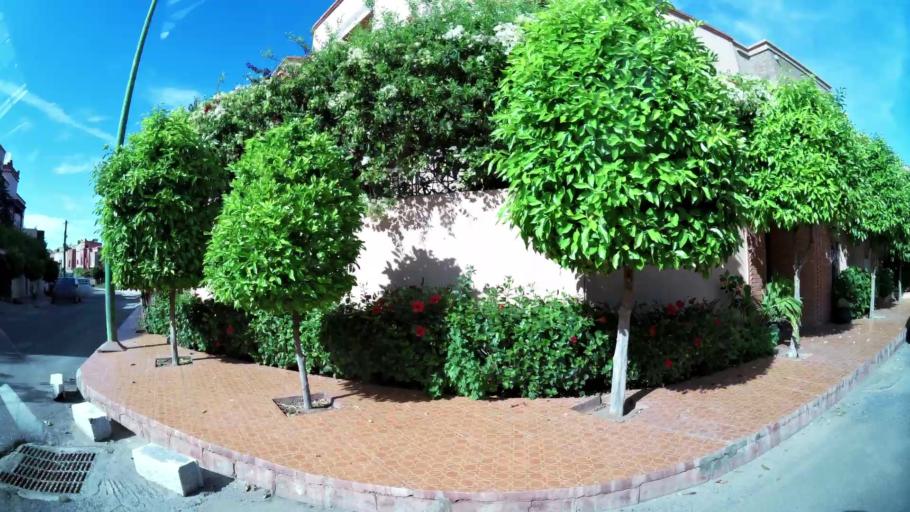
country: MA
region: Marrakech-Tensift-Al Haouz
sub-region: Marrakech
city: Marrakesh
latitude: 31.6460
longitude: -8.0432
